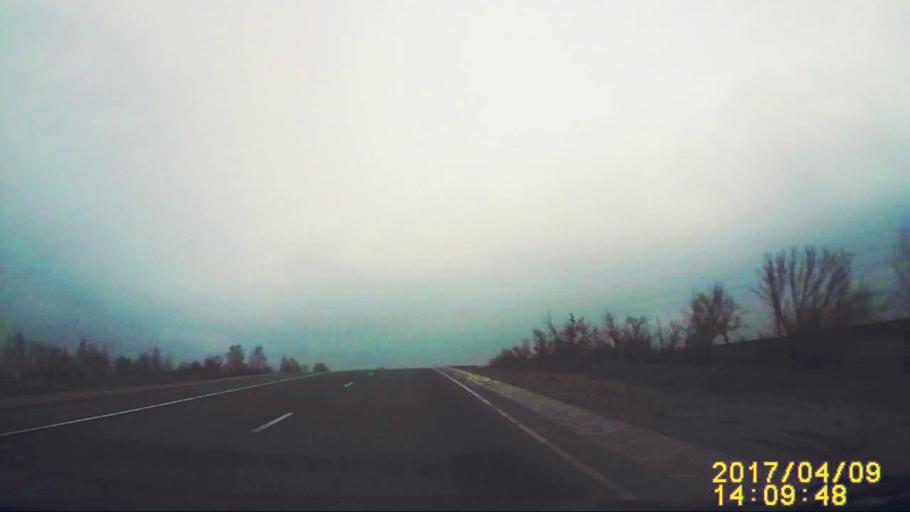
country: RU
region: Ulyanovsk
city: Krasnyy Gulyay
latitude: 54.0318
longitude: 48.2129
